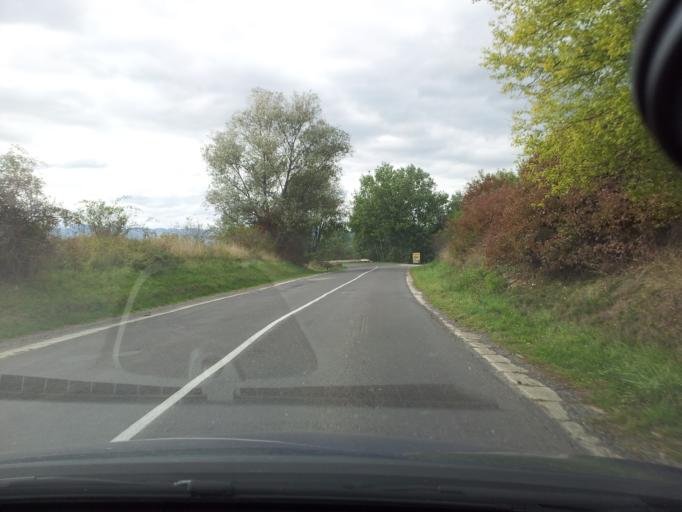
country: SK
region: Zilinsky
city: Ruzomberok
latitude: 49.1045
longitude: 19.4370
